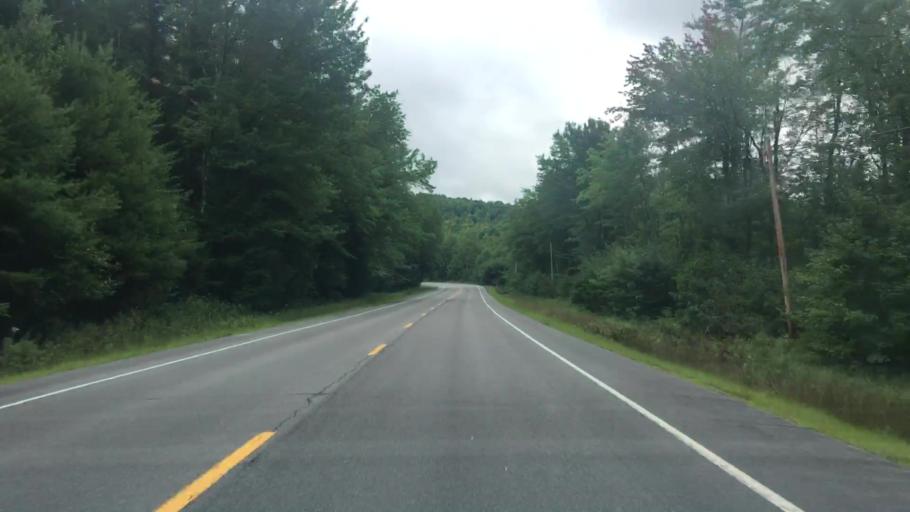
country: US
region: Maine
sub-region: York County
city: Cornish
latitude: 43.7816
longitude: -70.8240
